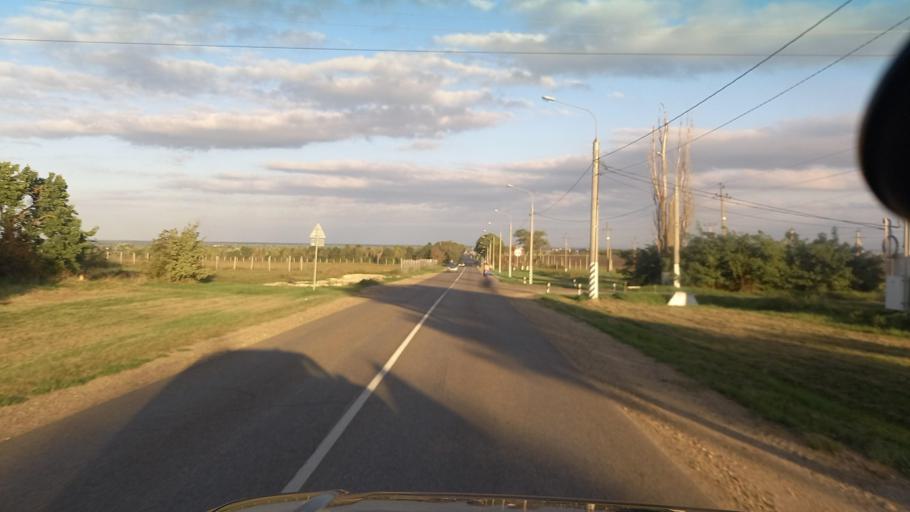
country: RU
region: Krasnodarskiy
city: Krymsk
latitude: 44.9389
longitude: 37.9448
